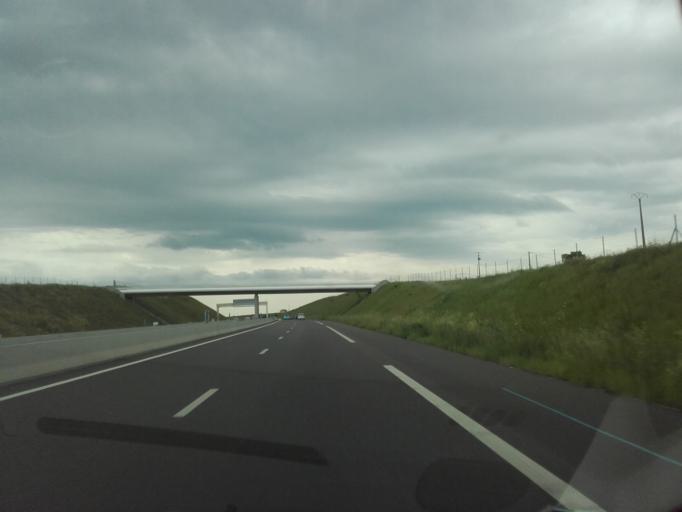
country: FR
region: Rhone-Alpes
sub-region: Departement du Rhone
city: Bully
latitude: 45.8704
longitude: 4.5547
